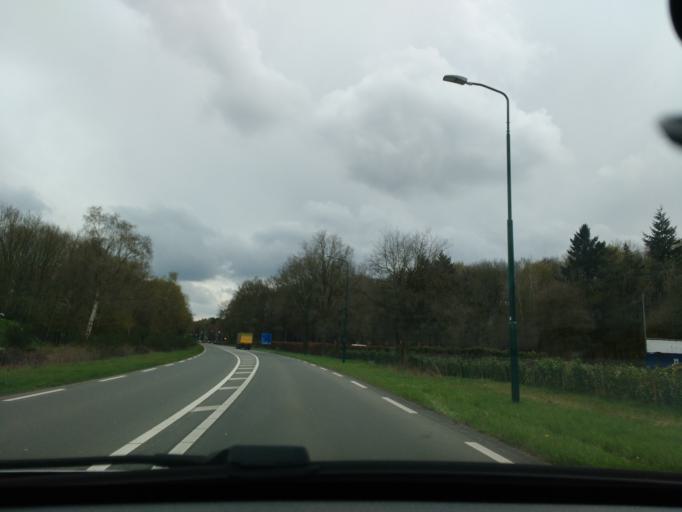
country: NL
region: Utrecht
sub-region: Gemeente Veenendaal
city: Veenendaal
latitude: 52.0084
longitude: 5.5366
